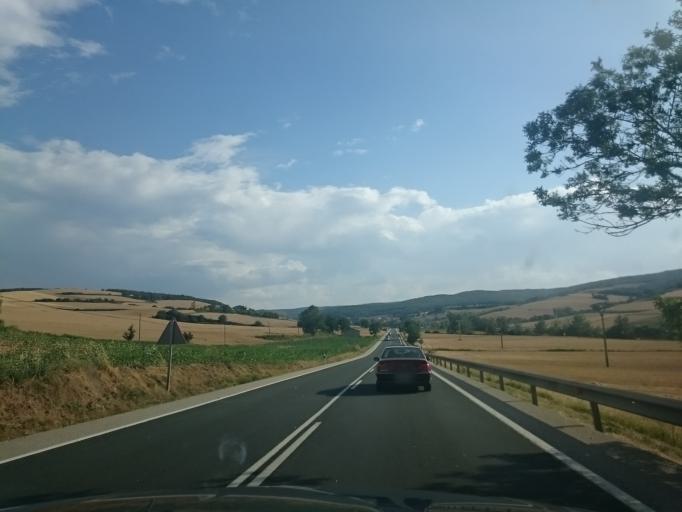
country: ES
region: Castille and Leon
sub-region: Provincia de Burgos
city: Espinosa del Camino
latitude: 42.3988
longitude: -3.2996
